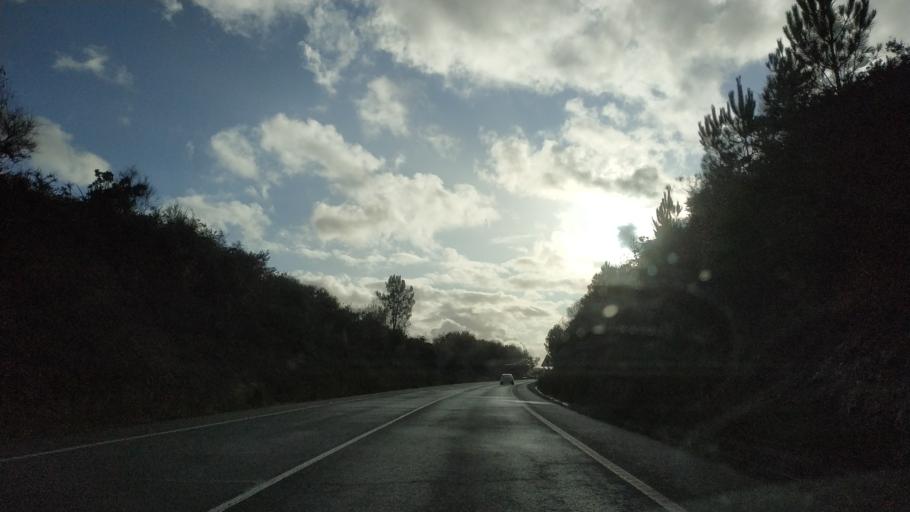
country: ES
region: Galicia
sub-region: Provincia da Coruna
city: Arzua
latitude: 42.8936
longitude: -8.1706
